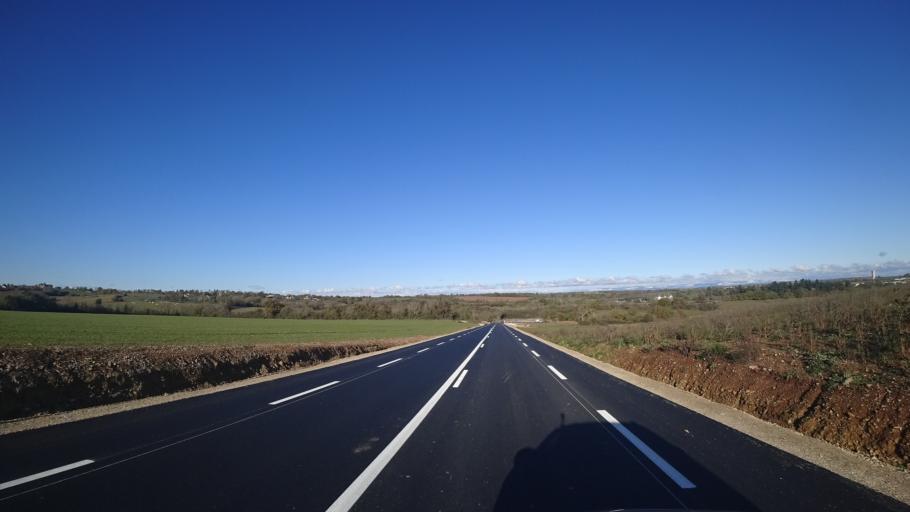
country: FR
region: Midi-Pyrenees
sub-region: Departement de l'Aveyron
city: Olemps
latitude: 44.3780
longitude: 2.5521
